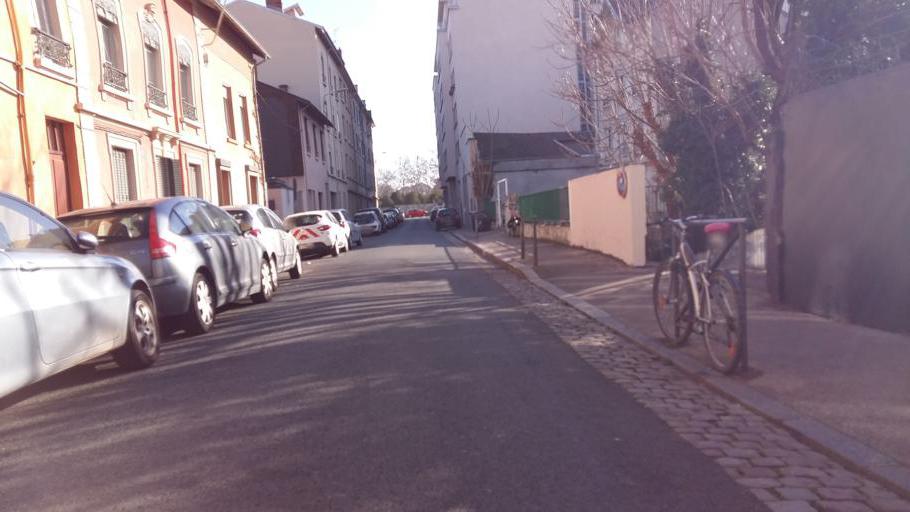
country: FR
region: Rhone-Alpes
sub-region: Departement du Rhone
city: Lyon
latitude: 45.7406
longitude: 4.8521
